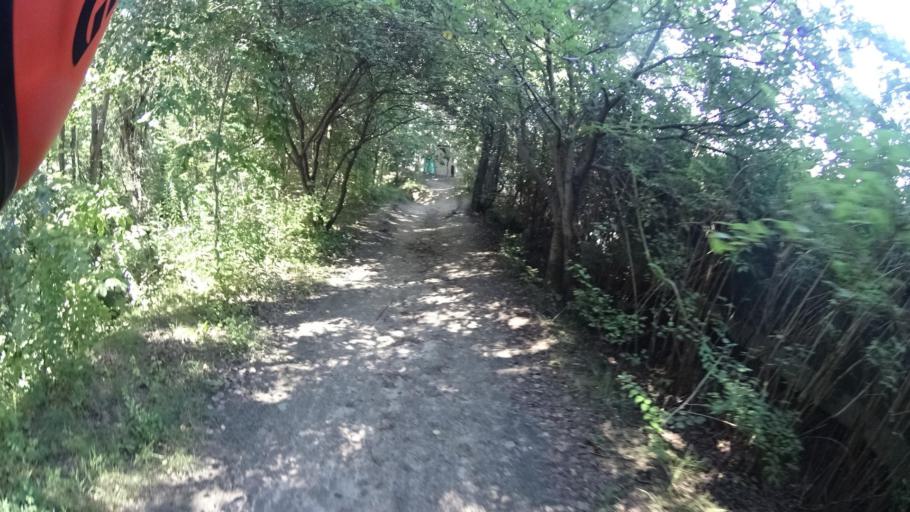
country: PL
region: Masovian Voivodeship
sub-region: Warszawa
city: Ursynow
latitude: 52.1258
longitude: 21.0561
